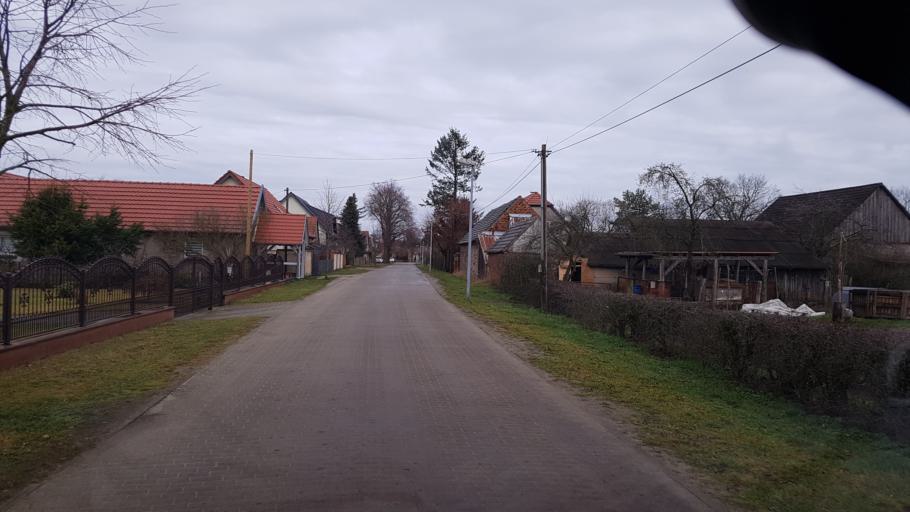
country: DE
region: Brandenburg
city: Altdobern
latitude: 51.6825
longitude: 14.0198
